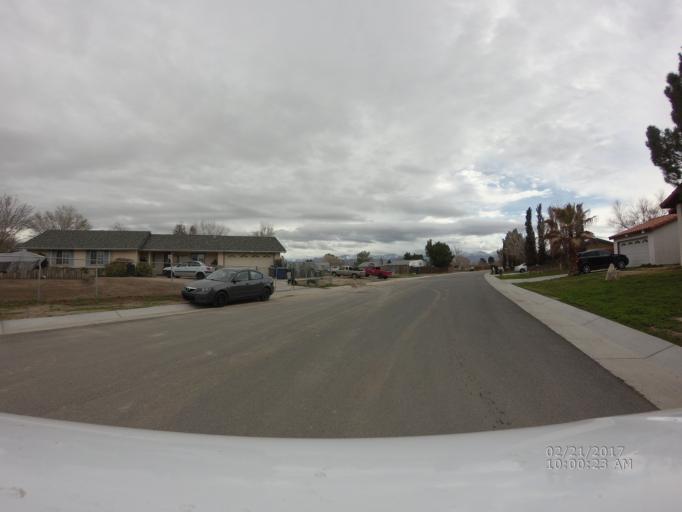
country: US
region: California
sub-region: Los Angeles County
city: Lake Los Angeles
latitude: 34.6031
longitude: -117.8229
